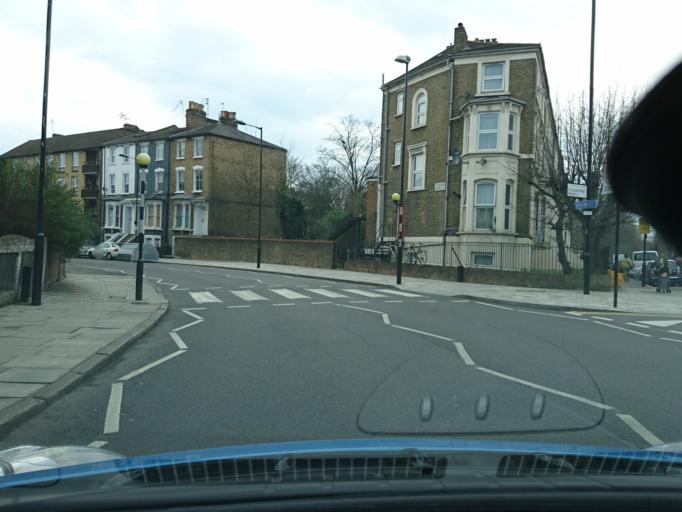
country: GB
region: England
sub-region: Greater London
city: Hackney
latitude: 51.5557
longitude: -0.0565
